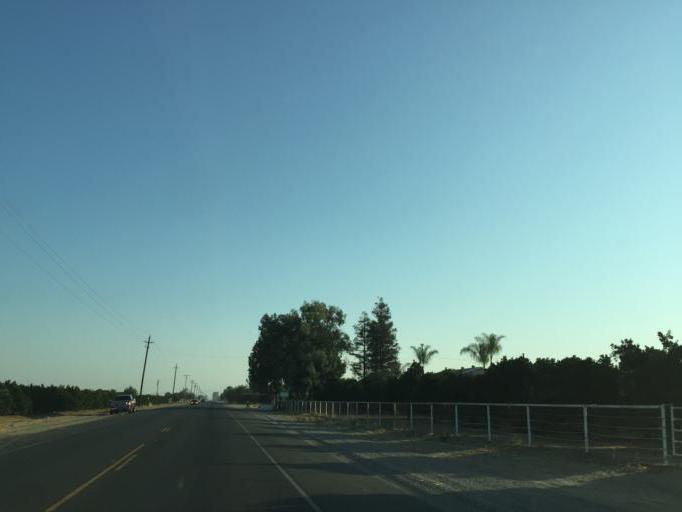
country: US
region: California
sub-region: Tulare County
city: Ivanhoe
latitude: 36.4296
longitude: -119.2958
